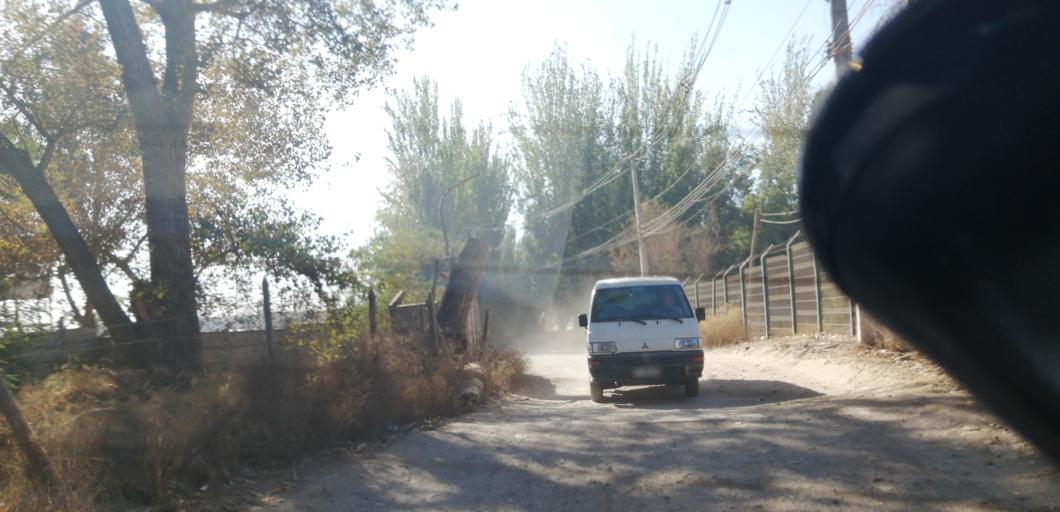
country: CL
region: Santiago Metropolitan
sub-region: Provincia de Santiago
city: Lo Prado
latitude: -33.4631
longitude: -70.7738
